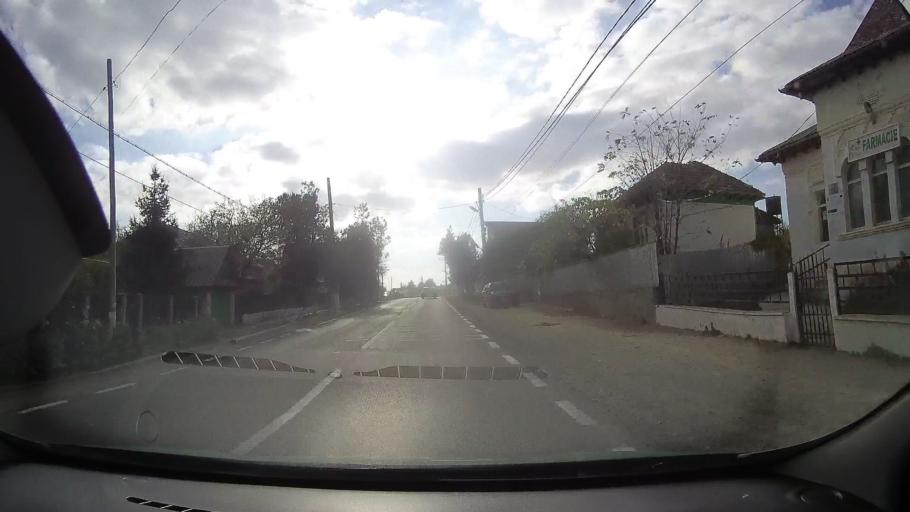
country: RO
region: Tulcea
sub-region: Comuna Topolog
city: Topolog
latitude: 44.8809
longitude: 28.3773
